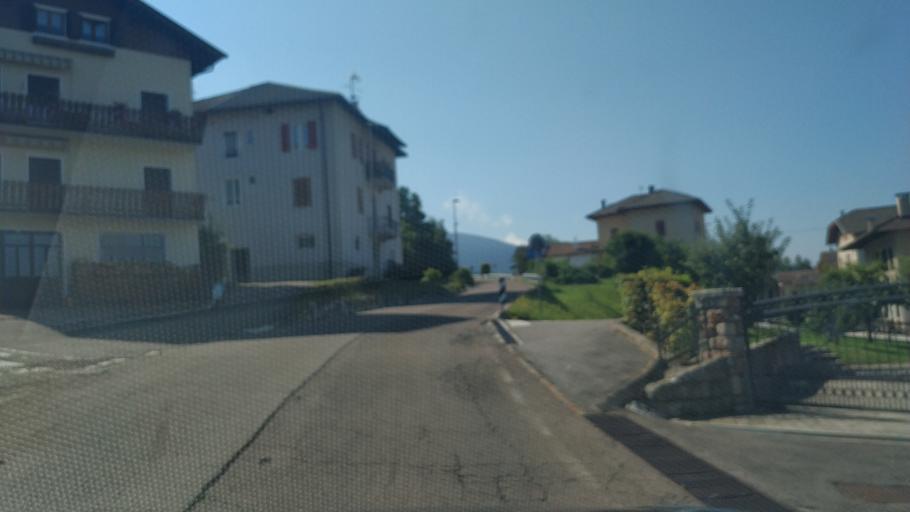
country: IT
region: Trentino-Alto Adige
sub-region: Provincia di Trento
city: Sarnonico
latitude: 46.4174
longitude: 11.1422
